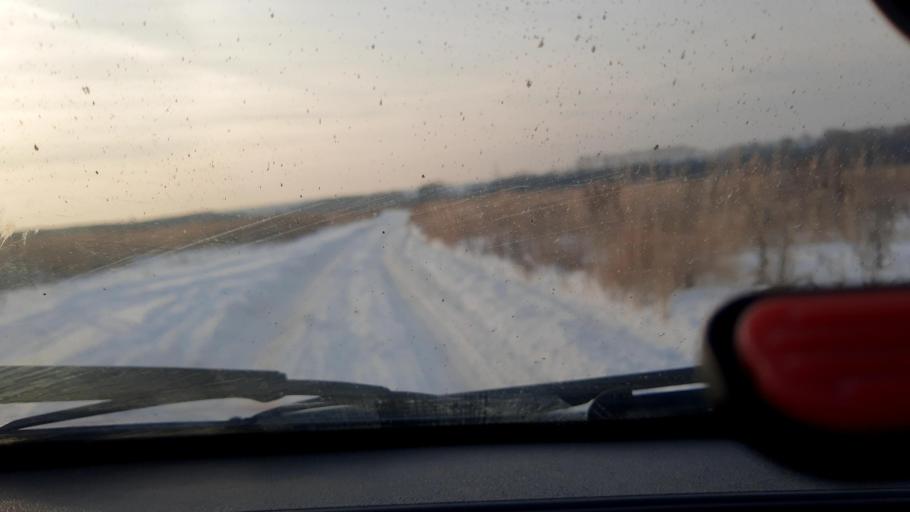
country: RU
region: Bashkortostan
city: Iglino
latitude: 54.7346
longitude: 56.2458
